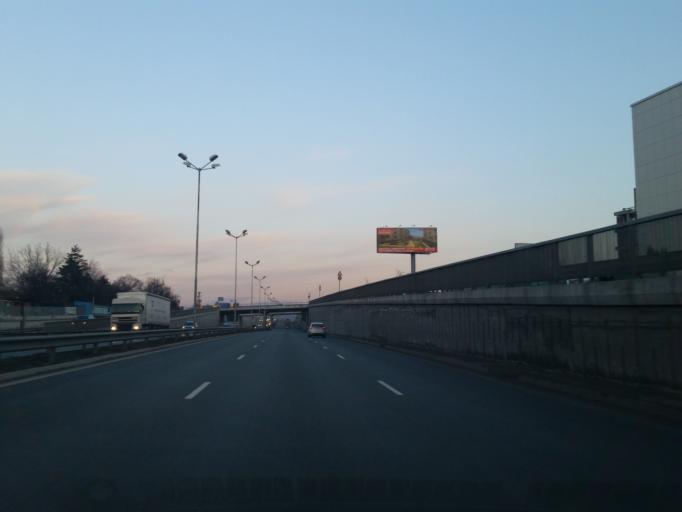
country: BG
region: Sofia-Capital
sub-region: Stolichna Obshtina
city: Sofia
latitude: 42.6428
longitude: 23.3096
